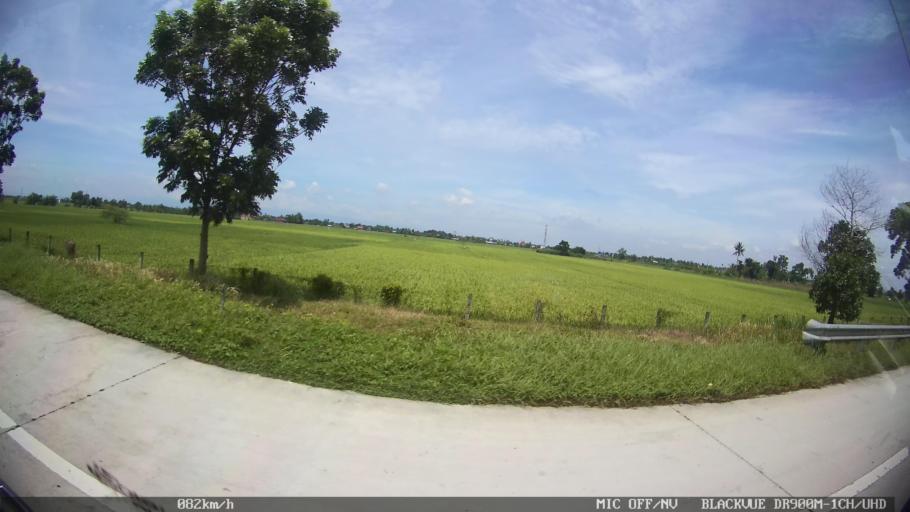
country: ID
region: North Sumatra
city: Perbaungan
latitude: 3.5441
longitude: 98.8907
